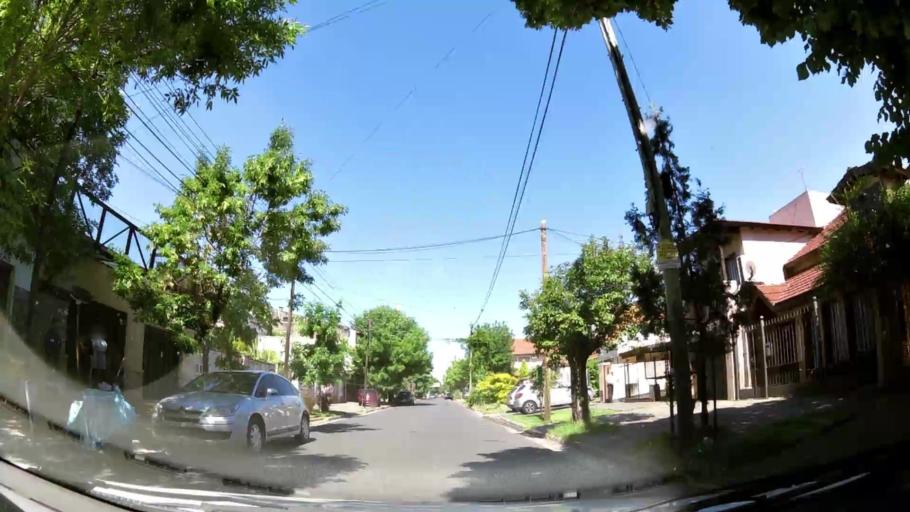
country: AR
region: Buenos Aires
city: Ituzaingo
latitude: -34.6543
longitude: -58.6657
